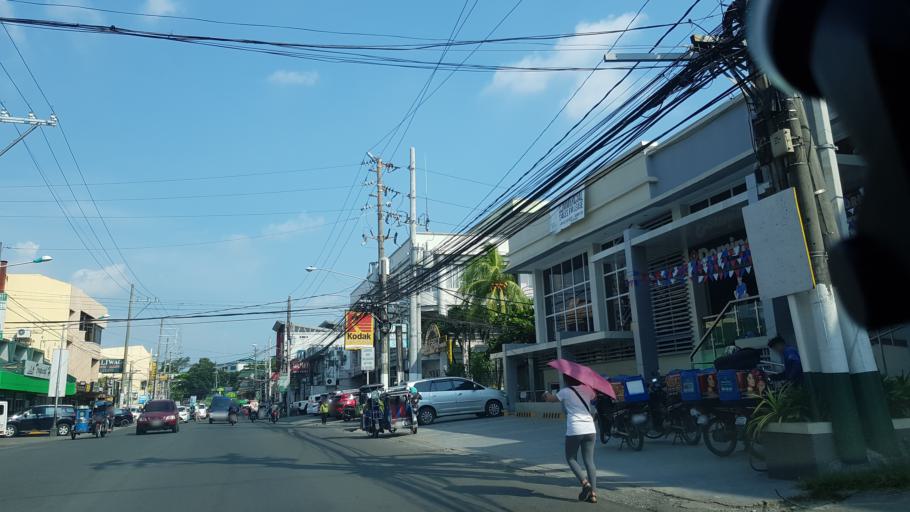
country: PH
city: Sambayanihan People's Village
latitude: 14.4829
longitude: 121.0354
